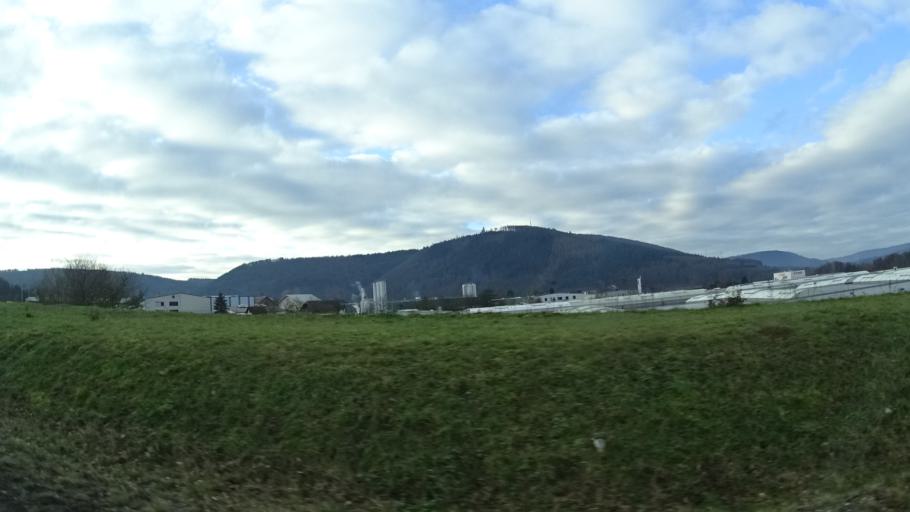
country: DE
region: Bavaria
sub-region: Regierungsbezirk Unterfranken
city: Faulbach
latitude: 49.7869
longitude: 9.4509
